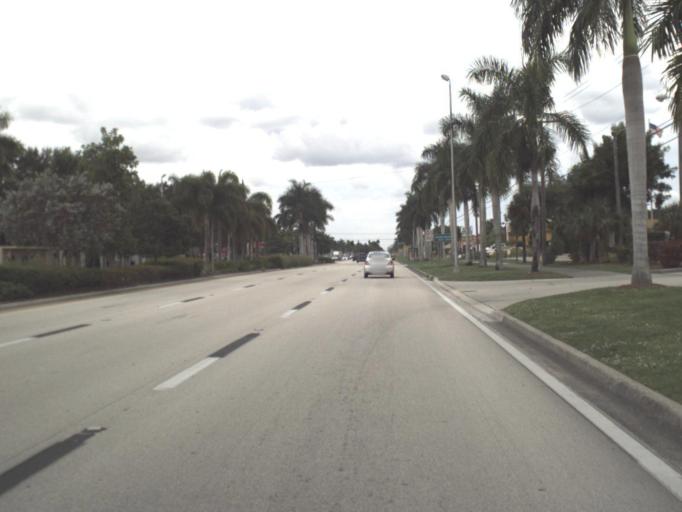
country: US
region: Florida
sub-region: Lee County
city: Tice
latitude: 26.6814
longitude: -81.8037
